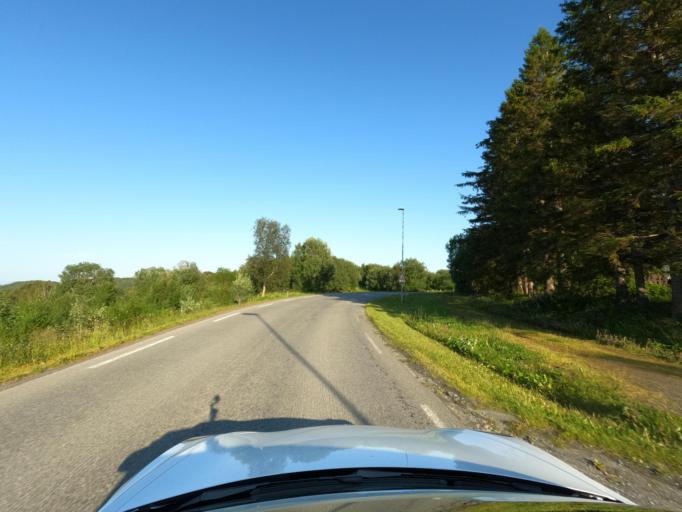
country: NO
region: Nordland
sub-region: Evenes
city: Randa
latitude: 68.4898
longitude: 16.8987
